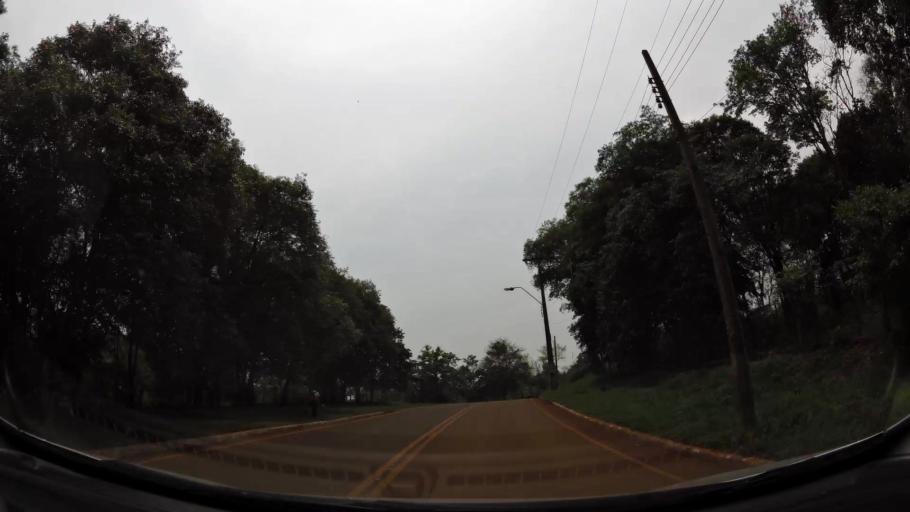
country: PY
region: Alto Parana
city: Presidente Franco
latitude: -25.5600
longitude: -54.6325
